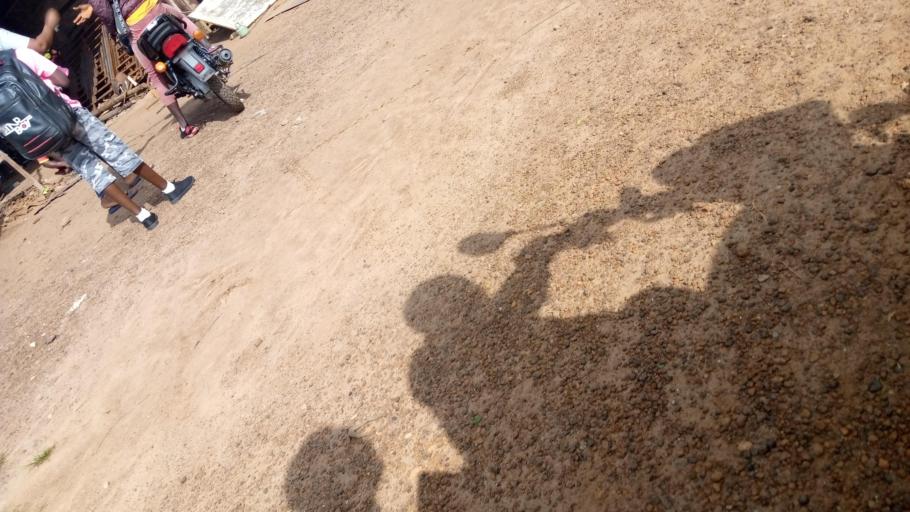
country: SL
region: Southern Province
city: Pujehun
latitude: 7.3575
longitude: -11.7237
